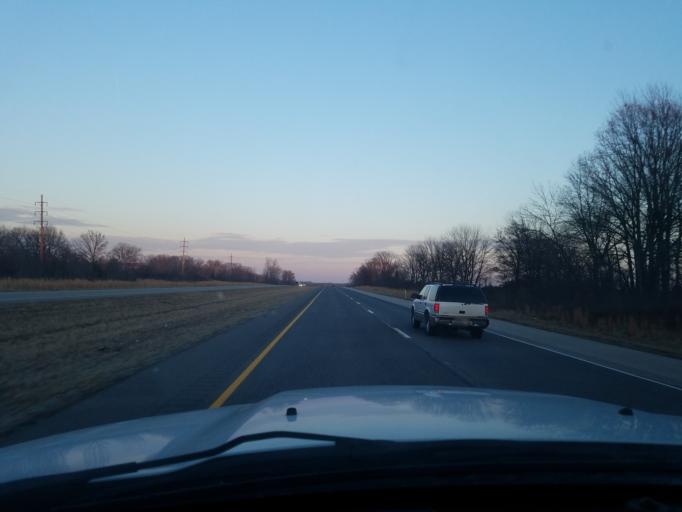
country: US
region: Indiana
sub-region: Warrick County
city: Boonville
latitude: 38.2001
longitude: -87.2519
